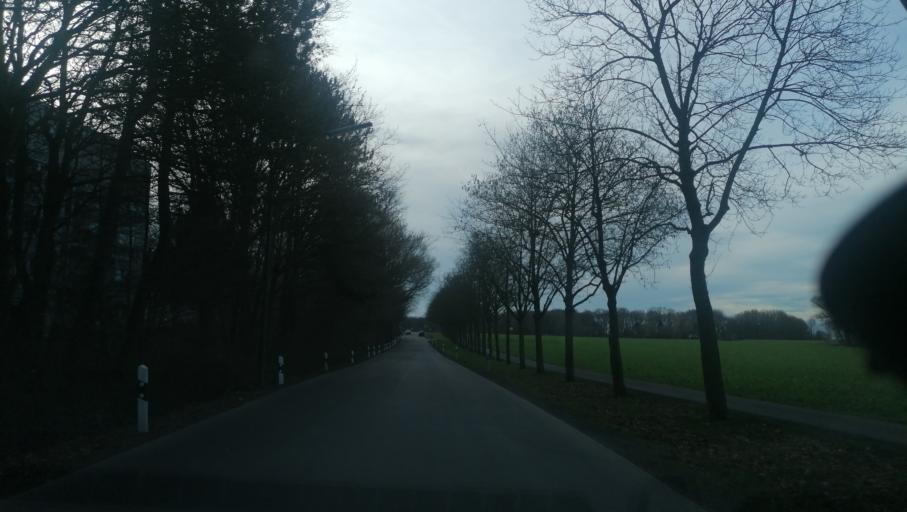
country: DE
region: North Rhine-Westphalia
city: Bergkamen
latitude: 51.6053
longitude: 7.6087
